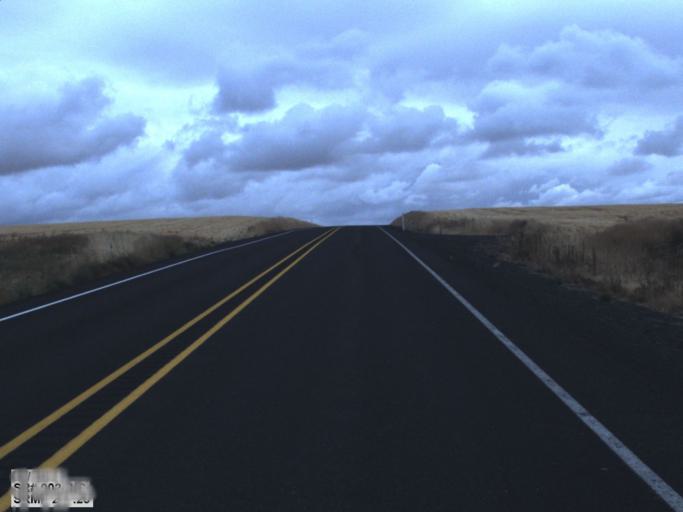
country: US
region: Washington
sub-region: Okanogan County
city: Coulee Dam
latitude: 47.7548
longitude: -118.7981
